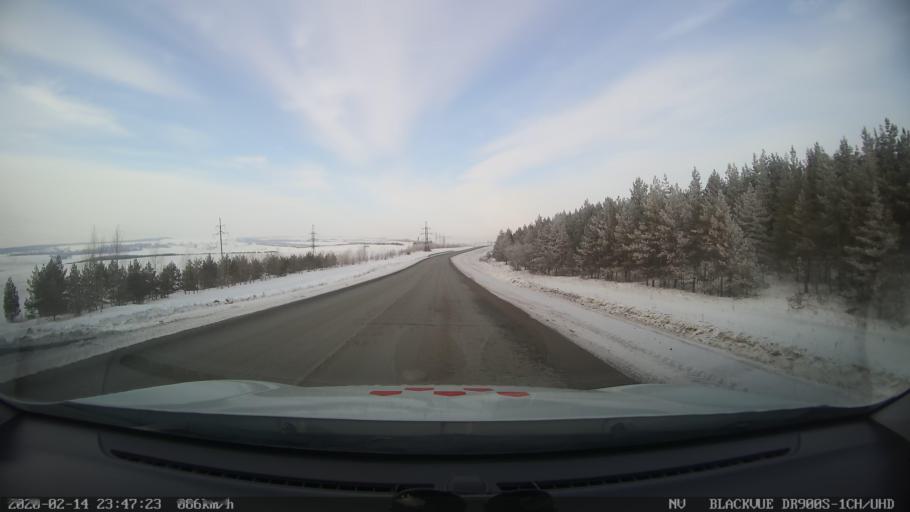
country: RU
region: Tatarstan
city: Kuybyshevskiy Zaton
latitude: 55.2379
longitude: 49.2095
